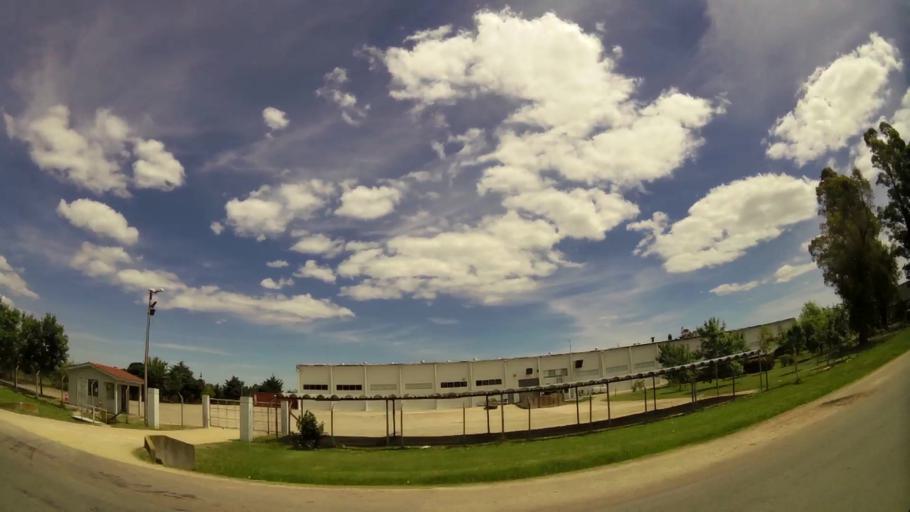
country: UY
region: San Jose
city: Delta del Tigre
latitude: -34.7421
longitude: -56.4338
